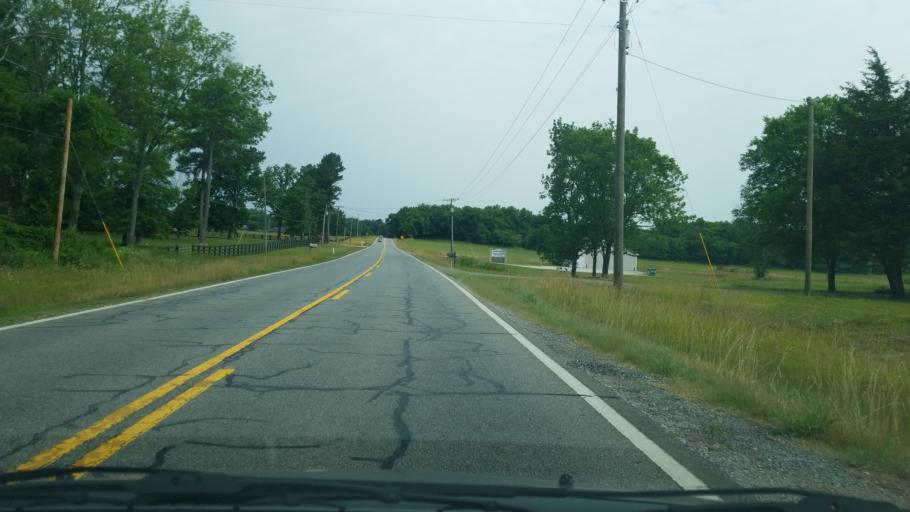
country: US
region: Georgia
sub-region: Catoosa County
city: Ringgold
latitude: 34.8543
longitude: -85.1430
